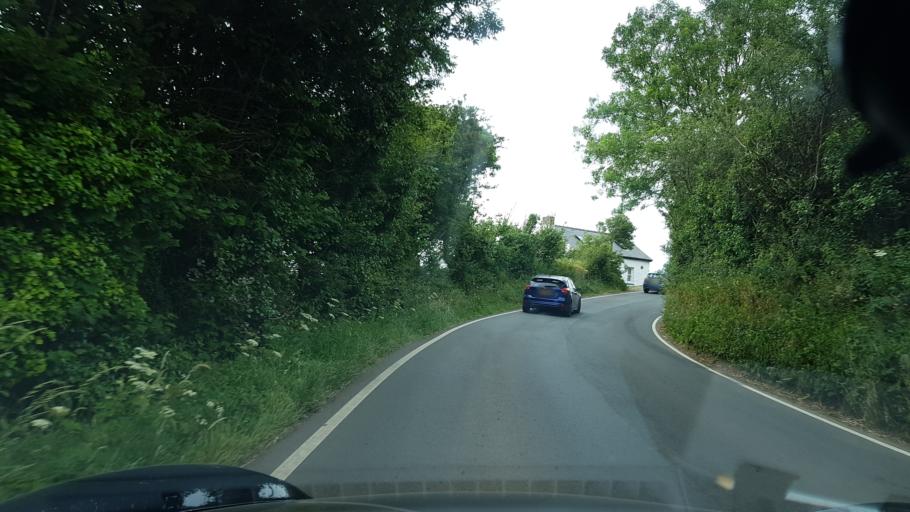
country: GB
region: Wales
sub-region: Pembrokeshire
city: Herbrandston
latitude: 51.7638
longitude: -5.0894
